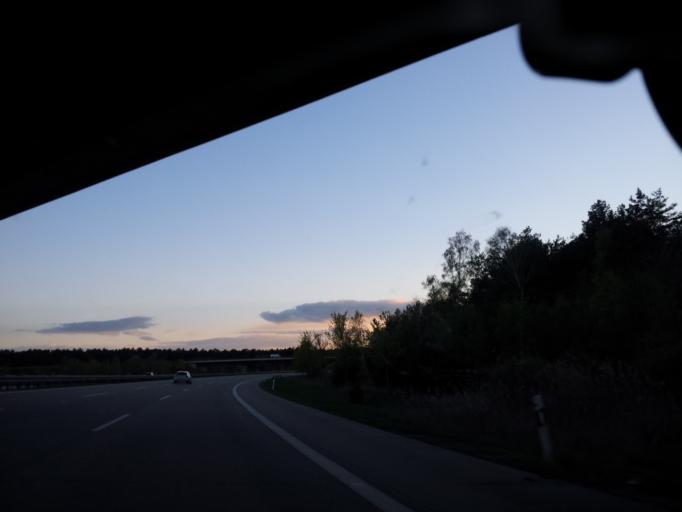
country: DE
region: Brandenburg
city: Erkner
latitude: 52.3269
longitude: 13.7486
